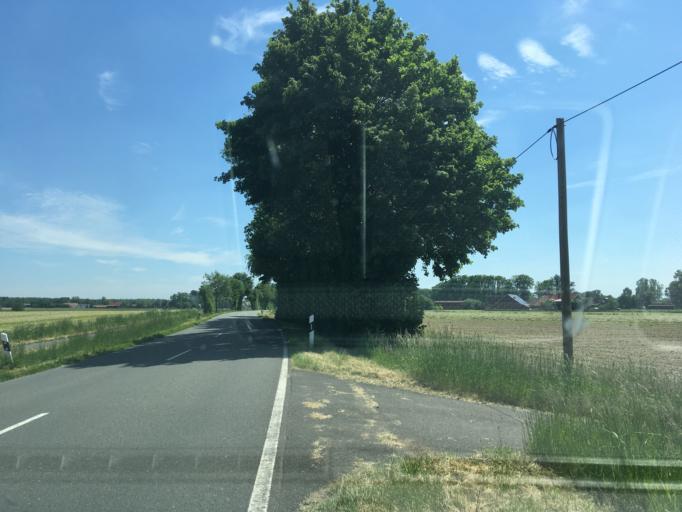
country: DE
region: North Rhine-Westphalia
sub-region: Regierungsbezirk Munster
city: Borken
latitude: 51.8837
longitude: 6.8224
